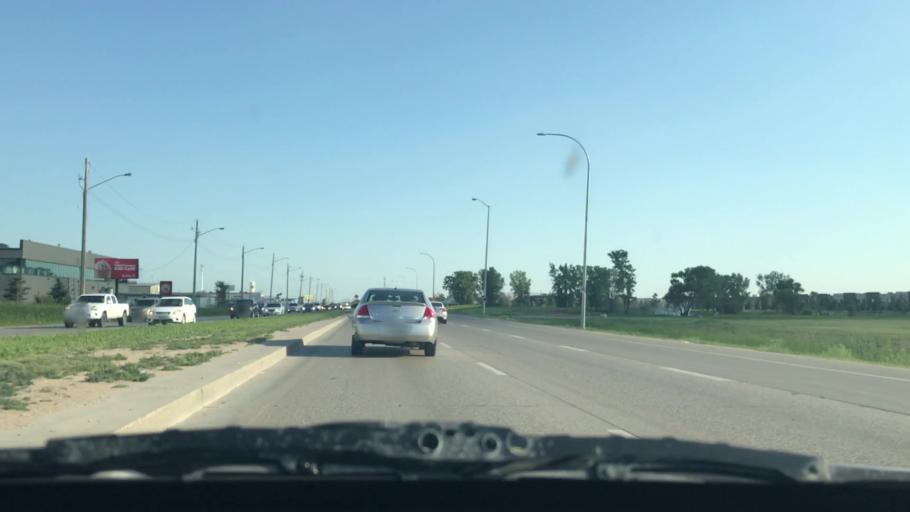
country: CA
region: Manitoba
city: Winnipeg
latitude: 49.8375
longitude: -97.2093
